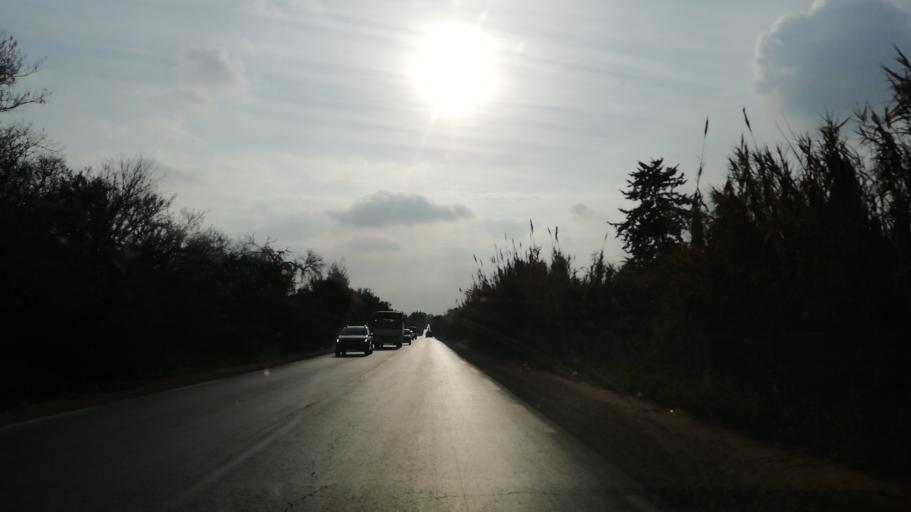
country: DZ
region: Mostaganem
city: Mostaganem
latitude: 35.8366
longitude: 0.0598
